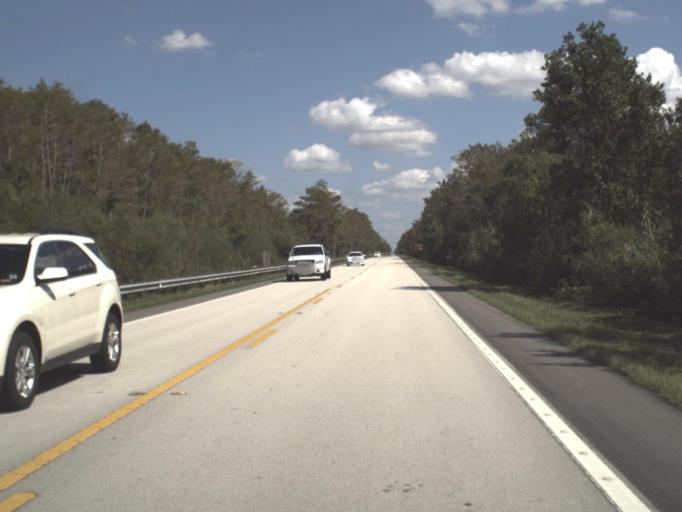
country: US
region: Florida
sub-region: Miami-Dade County
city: Kendall West
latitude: 25.8566
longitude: -81.0307
